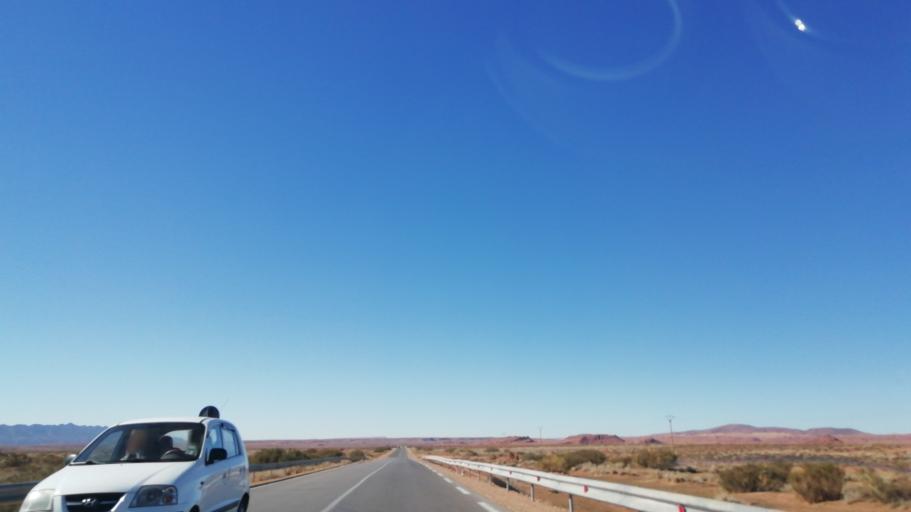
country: DZ
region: El Bayadh
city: El Abiodh Sidi Cheikh
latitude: 33.1839
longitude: 0.5574
